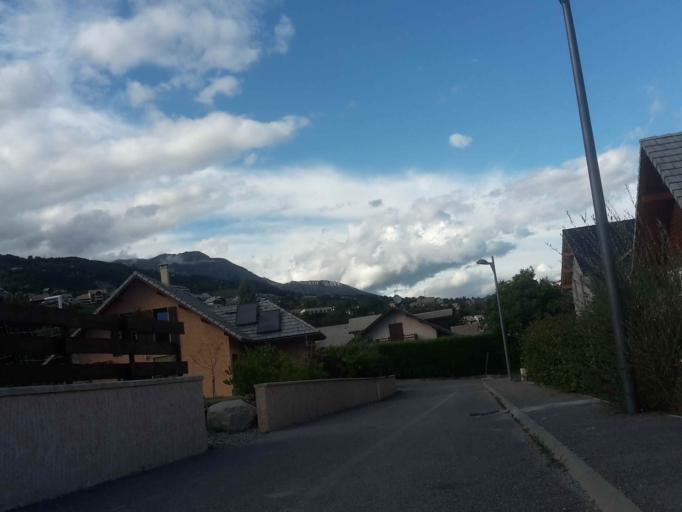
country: FR
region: Provence-Alpes-Cote d'Azur
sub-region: Departement des Hautes-Alpes
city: Embrun
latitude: 44.5545
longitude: 6.4854
